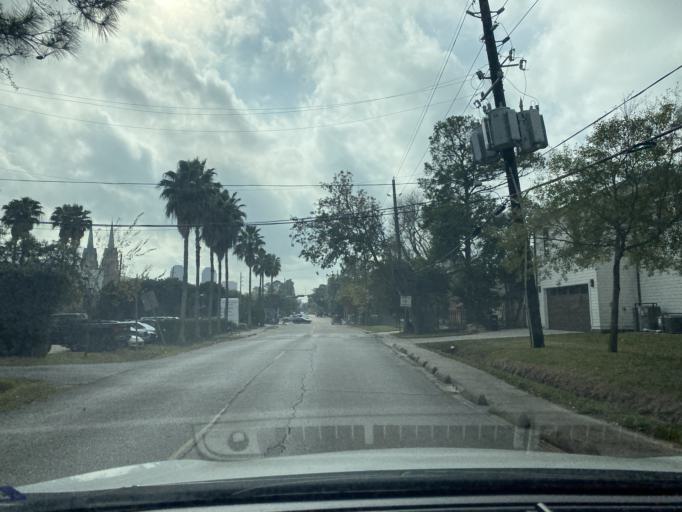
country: US
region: Texas
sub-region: Harris County
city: Hunters Creek Village
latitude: 29.7641
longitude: -95.4677
